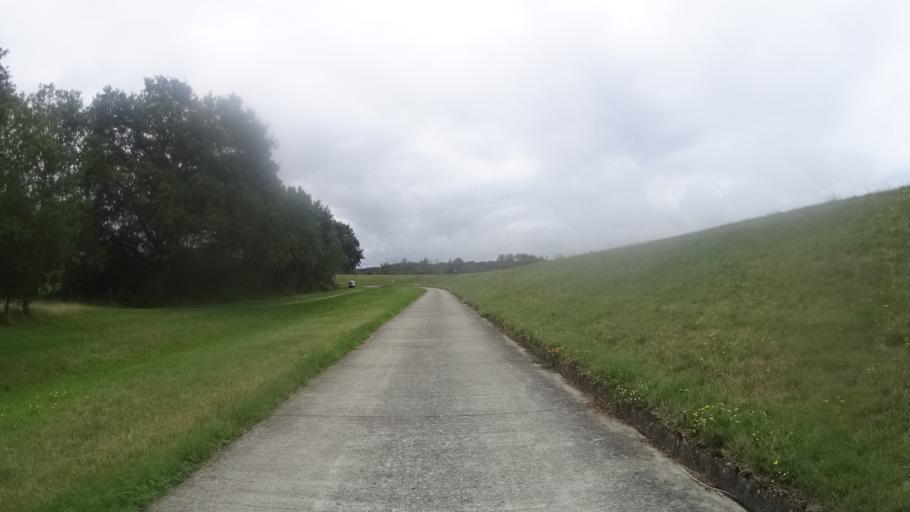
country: DE
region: Lower Saxony
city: Tosterglope
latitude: 53.2606
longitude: 10.8312
